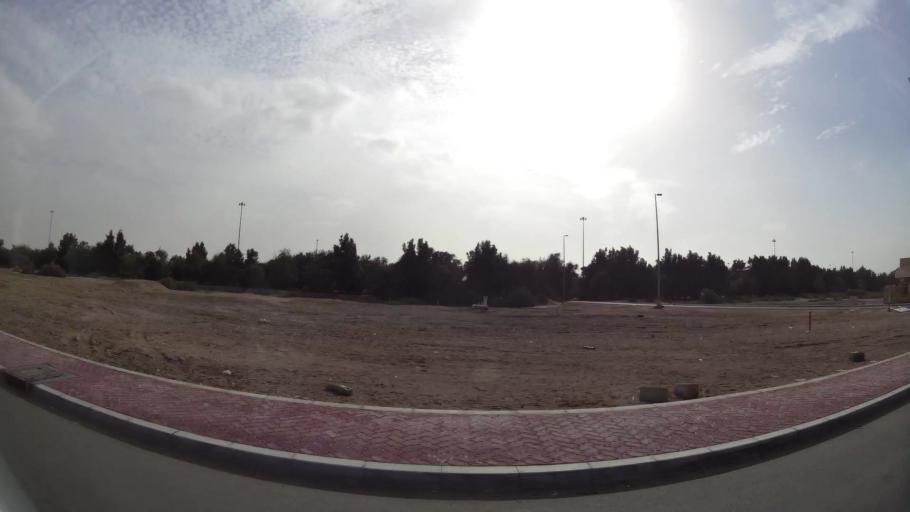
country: AE
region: Abu Dhabi
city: Abu Dhabi
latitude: 24.4062
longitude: 54.5259
